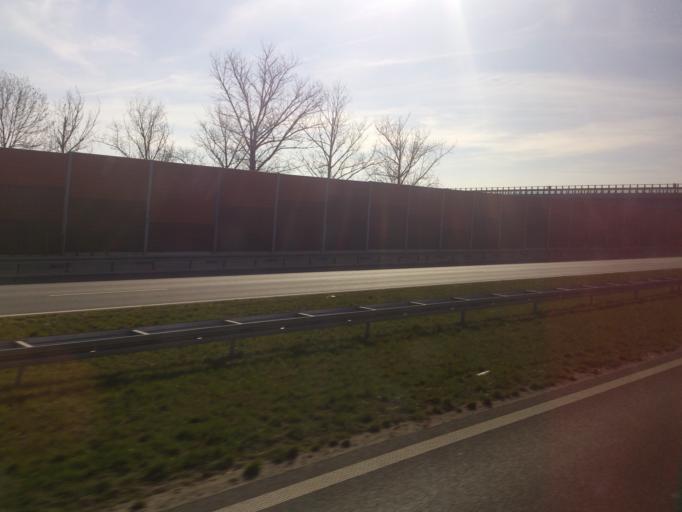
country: PL
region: Kujawsko-Pomorskie
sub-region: Powiat aleksandrowski
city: Raciazek
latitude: 52.8096
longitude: 18.8142
